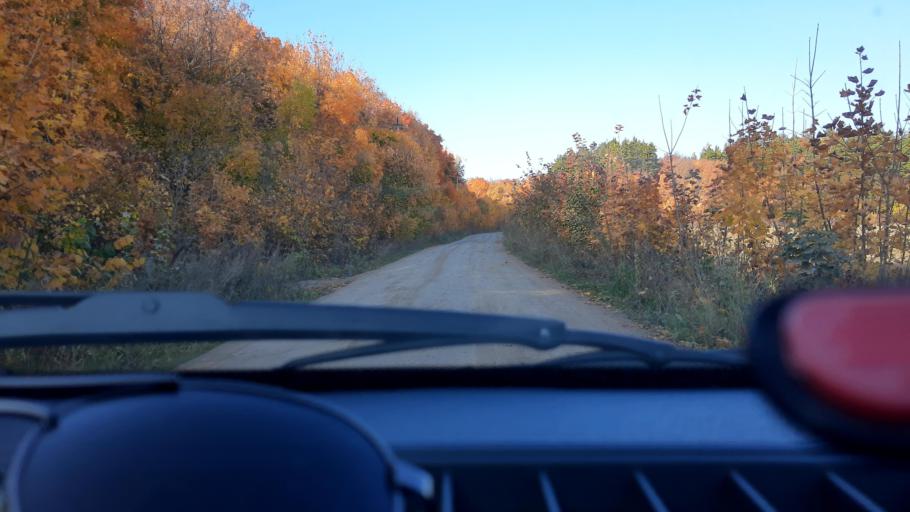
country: RU
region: Bashkortostan
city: Karmaskaly
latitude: 54.3758
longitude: 55.9105
